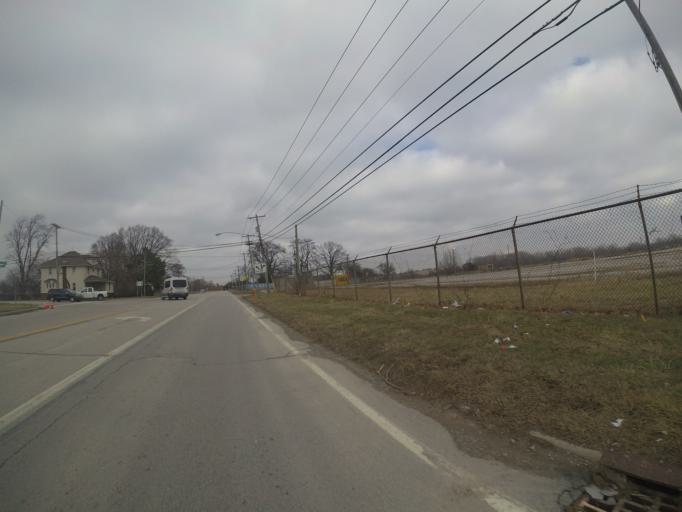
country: US
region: Ohio
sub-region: Wood County
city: Walbridge
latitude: 41.6154
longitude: -83.5125
